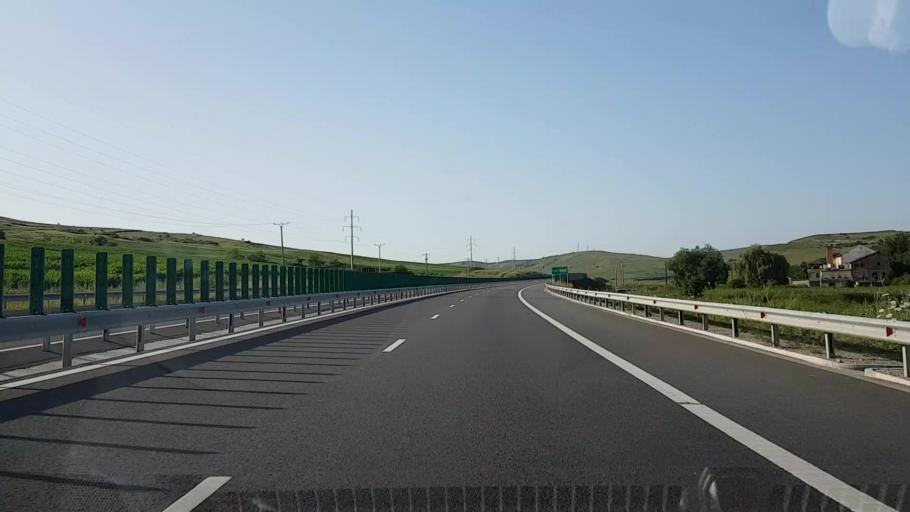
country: RO
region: Cluj
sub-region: Comuna Mihai Viteazu
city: Mihai Viteazu
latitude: 46.4724
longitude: 23.7759
